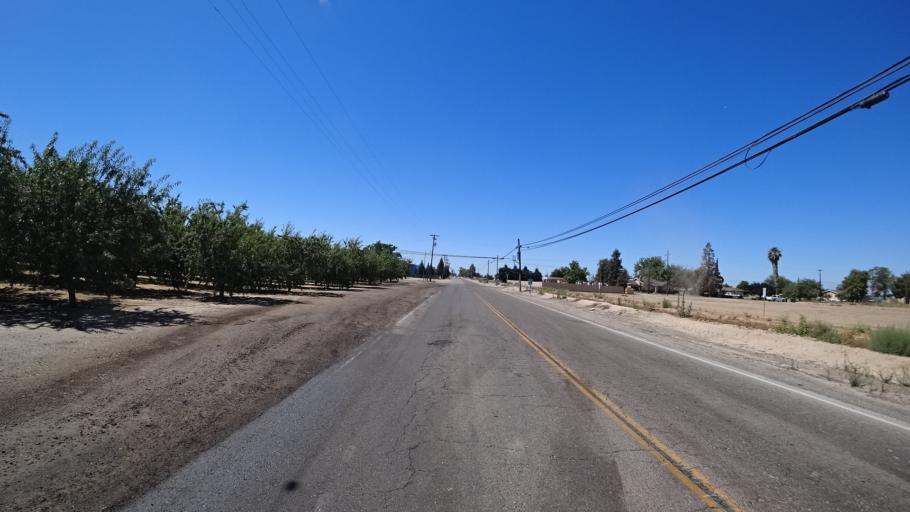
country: US
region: California
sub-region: Fresno County
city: Easton
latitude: 36.6714
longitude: -119.7458
